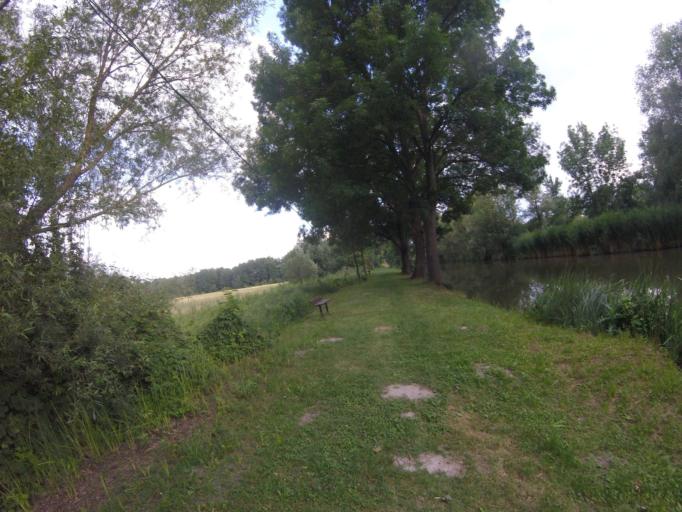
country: HU
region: Pest
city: Albertirsa
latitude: 47.2585
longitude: 19.6010
